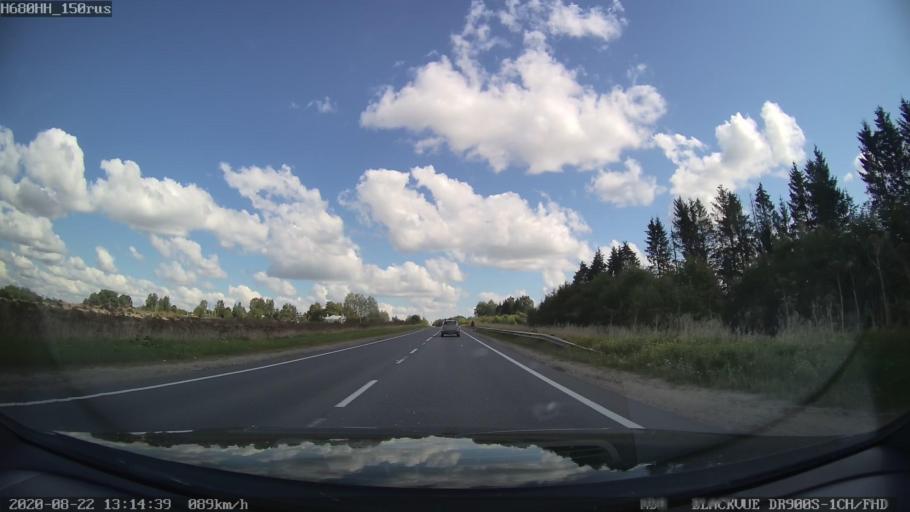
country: RU
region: Tverskaya
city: Bezhetsk
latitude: 57.7554
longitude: 36.6075
